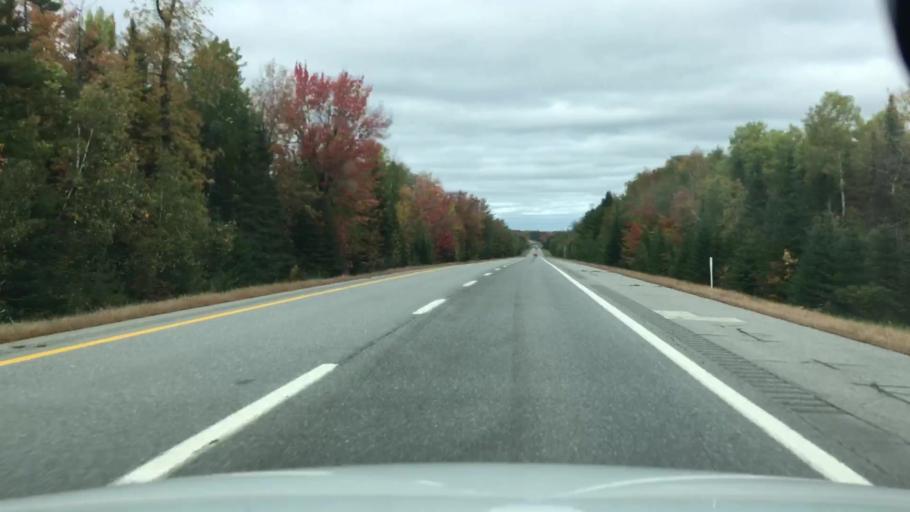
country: US
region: Maine
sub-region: Waldo County
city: Burnham
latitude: 44.6950
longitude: -69.4661
